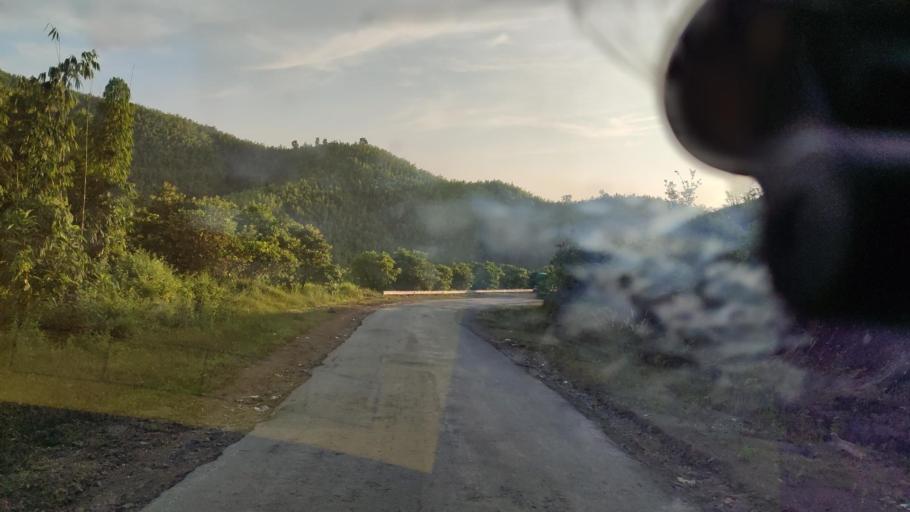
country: MM
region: Magway
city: Minbu
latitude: 19.8374
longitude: 94.1053
